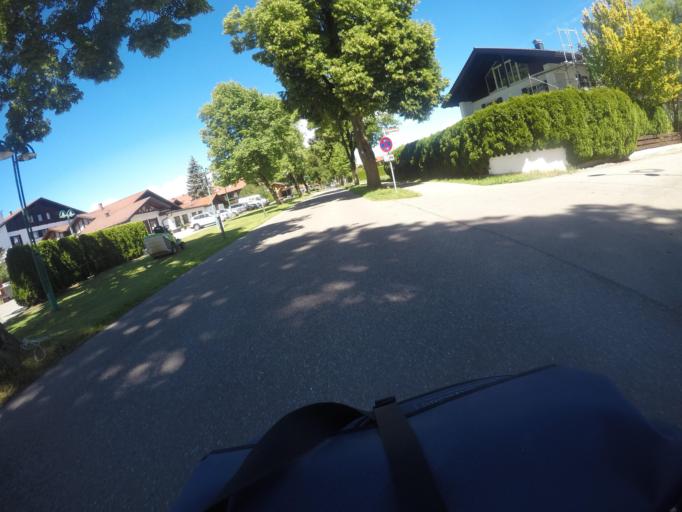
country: DE
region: Bavaria
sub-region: Swabia
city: Schwangau
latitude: 47.5821
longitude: 10.7320
